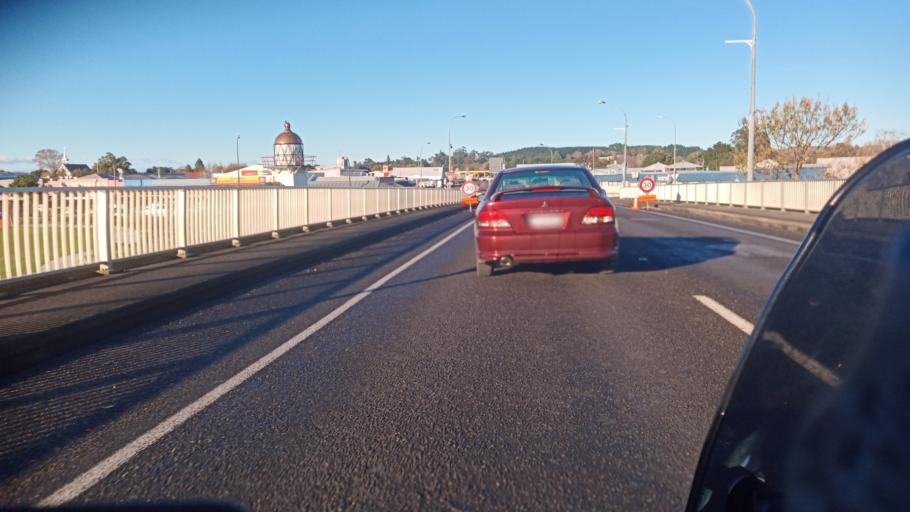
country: NZ
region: Hawke's Bay
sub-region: Wairoa District
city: Wairoa
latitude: -39.0321
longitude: 177.4186
